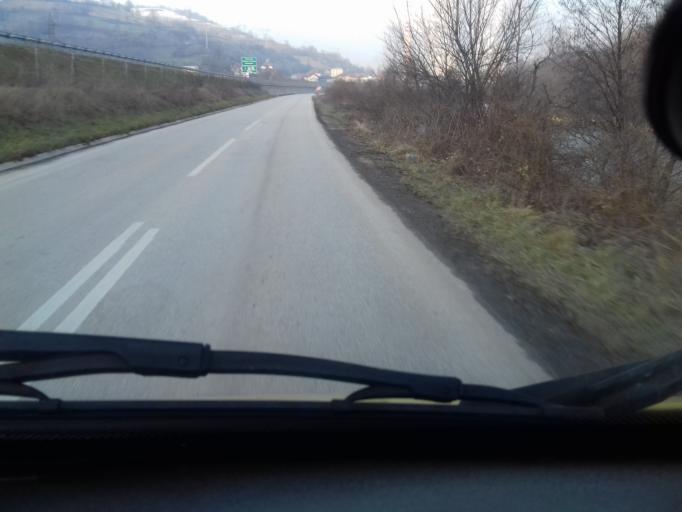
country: BA
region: Federation of Bosnia and Herzegovina
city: Dobrinje
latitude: 44.0745
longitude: 18.1083
